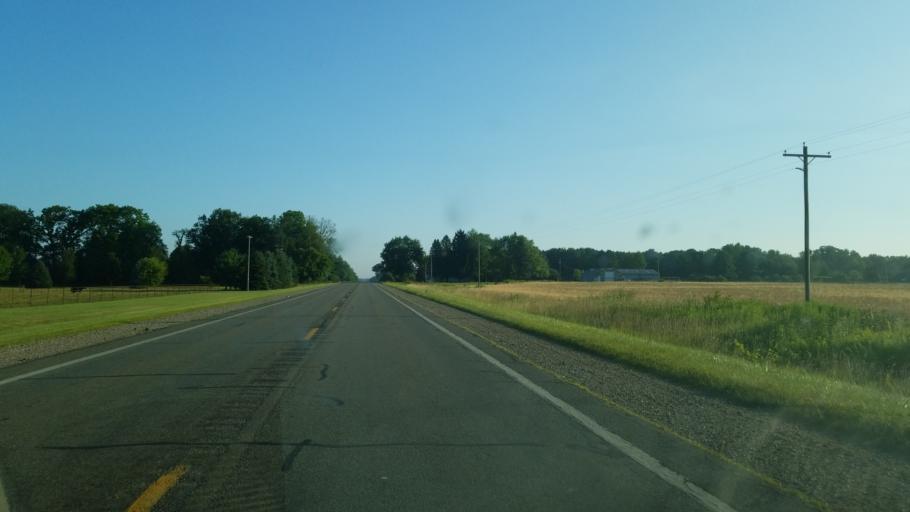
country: US
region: Michigan
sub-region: Montcalm County
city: Edmore
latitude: 43.3914
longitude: -85.0847
